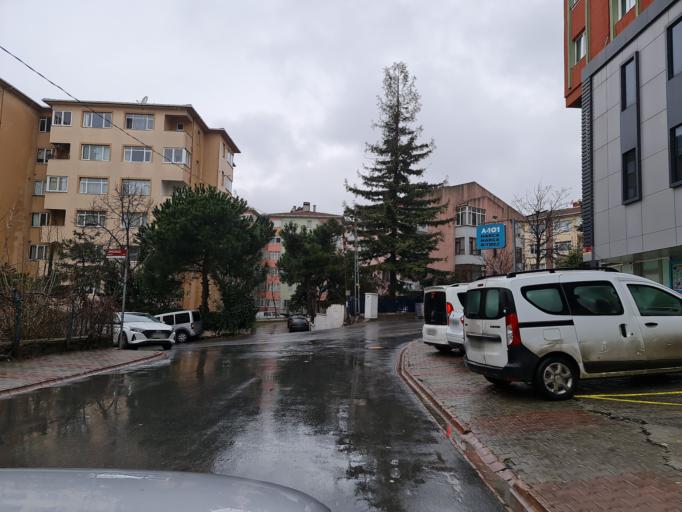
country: TR
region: Istanbul
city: Umraniye
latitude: 41.0094
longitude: 29.1023
